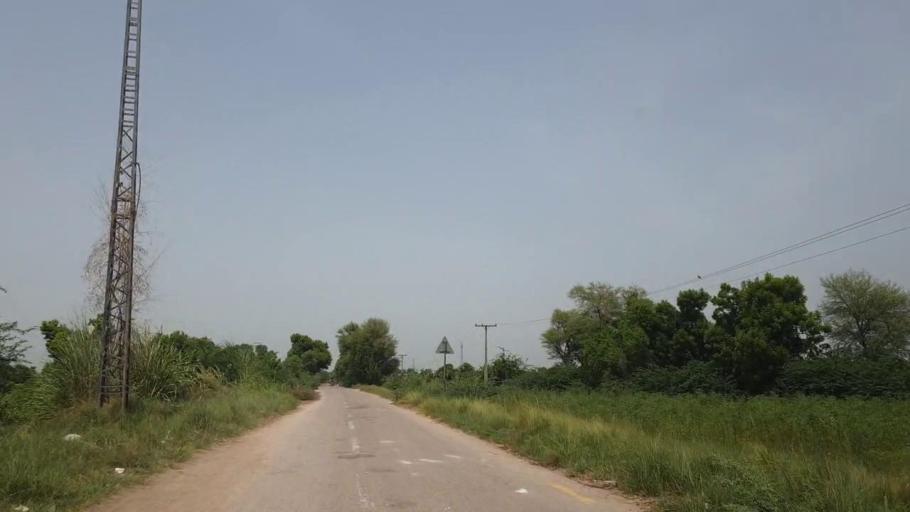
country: PK
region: Sindh
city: Sakrand
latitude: 26.1996
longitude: 68.2414
